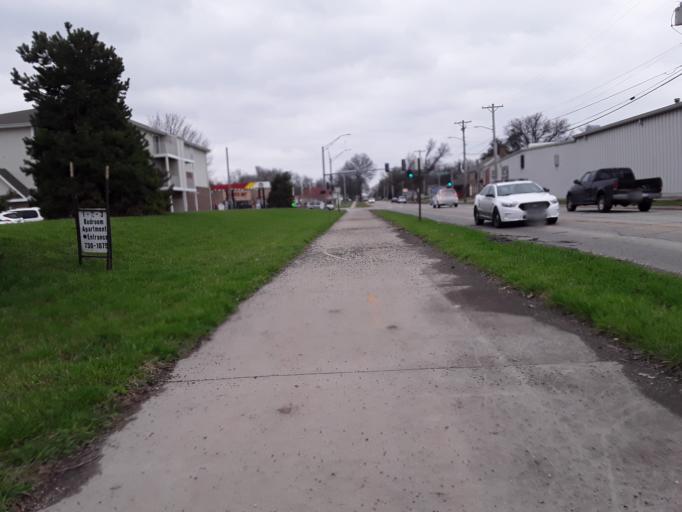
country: US
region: Nebraska
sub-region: Lancaster County
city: Lincoln
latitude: 40.8495
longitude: -96.6535
